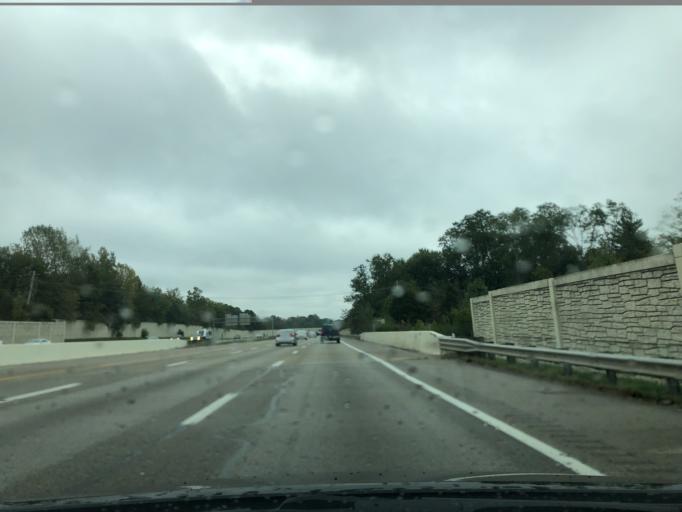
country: US
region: Ohio
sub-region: Hamilton County
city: Sixteen Mile Stand
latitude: 39.2523
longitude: -84.3223
